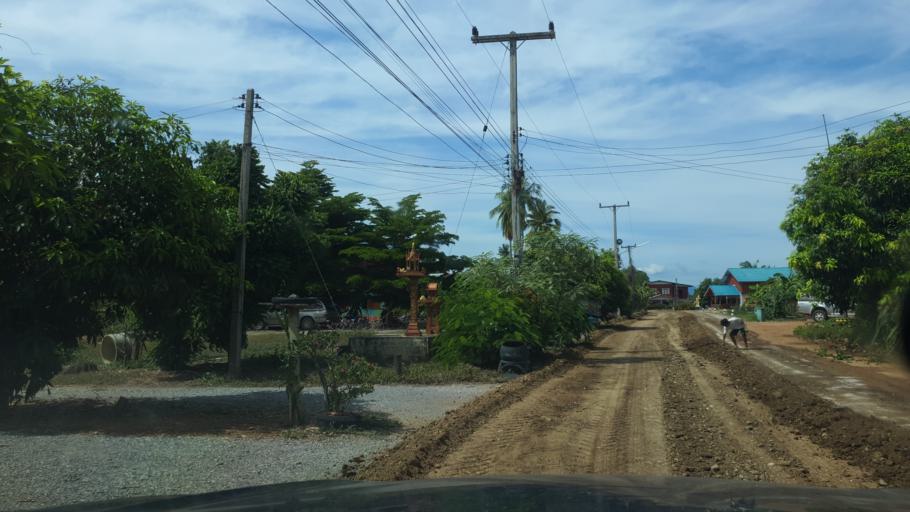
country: TH
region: Sukhothai
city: Si Samrong
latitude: 17.2043
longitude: 99.7207
